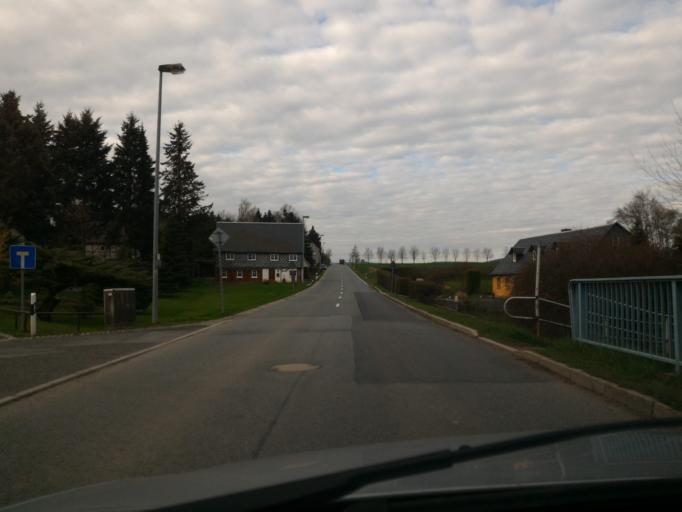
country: DE
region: Saxony
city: Hainewalde
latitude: 50.9508
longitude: 14.7226
